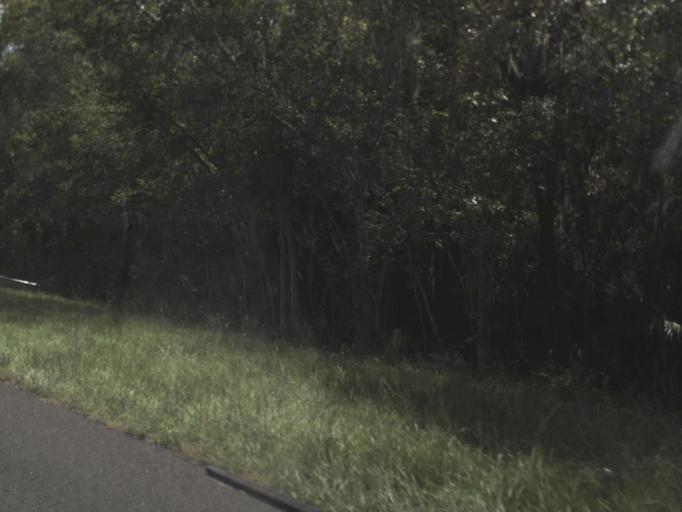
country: US
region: Florida
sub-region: Polk County
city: Willow Oak
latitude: 27.9241
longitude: -82.0311
